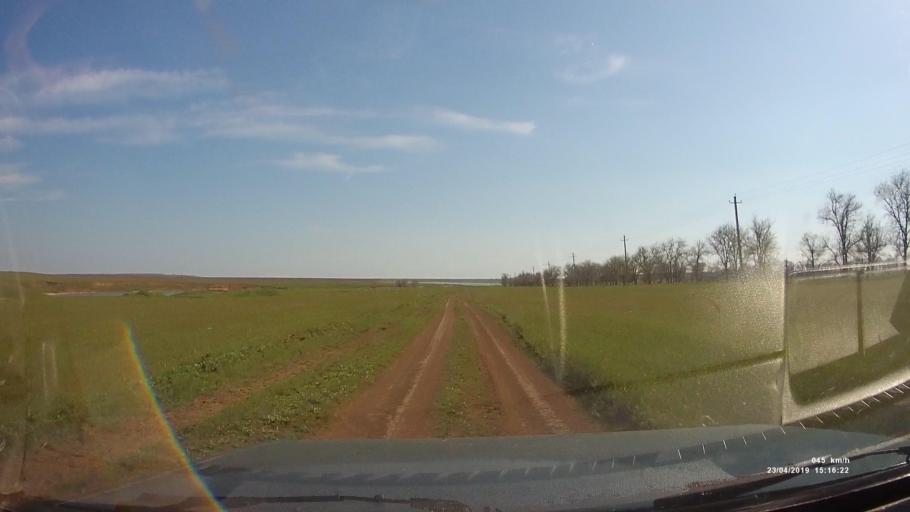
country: RU
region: Rostov
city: Remontnoye
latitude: 46.5340
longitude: 42.9696
